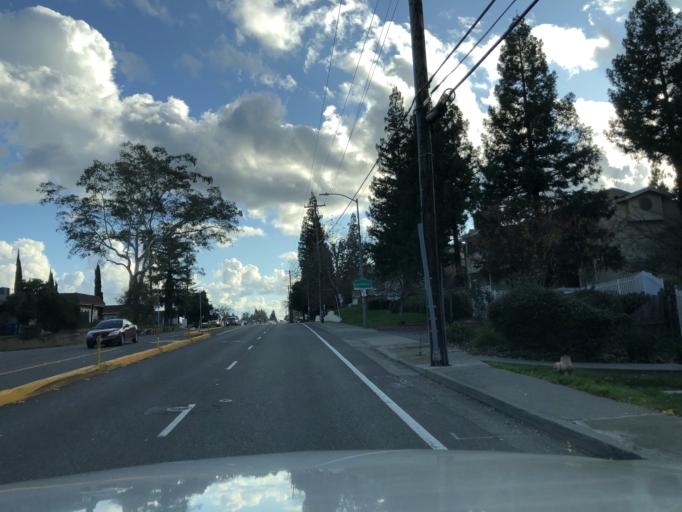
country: US
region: California
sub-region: Sacramento County
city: Foothill Farms
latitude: 38.6537
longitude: -121.3277
